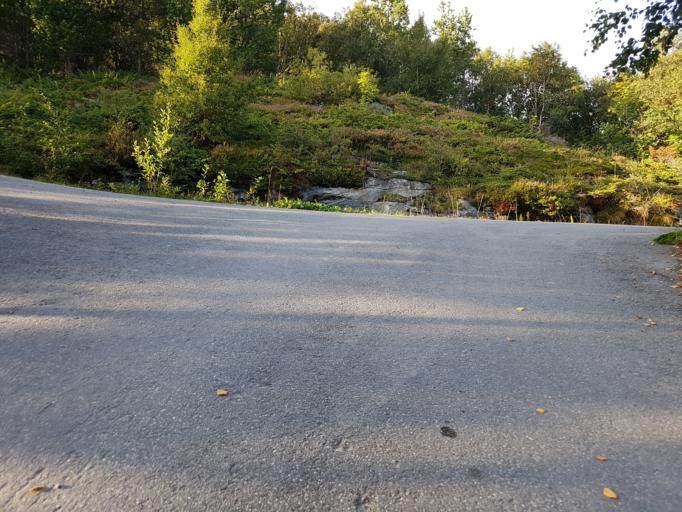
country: NO
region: Sor-Trondelag
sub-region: Afjord
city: A i Afjord
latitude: 64.0550
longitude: 9.9536
